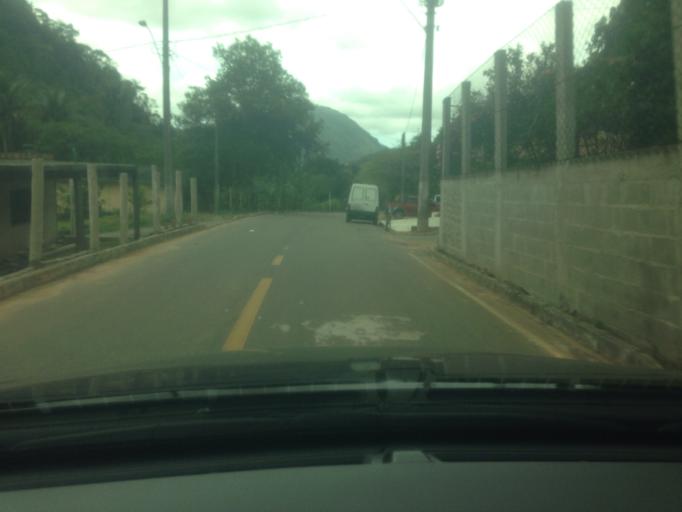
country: BR
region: Espirito Santo
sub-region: Guarapari
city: Guarapari
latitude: -20.5569
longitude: -40.5544
